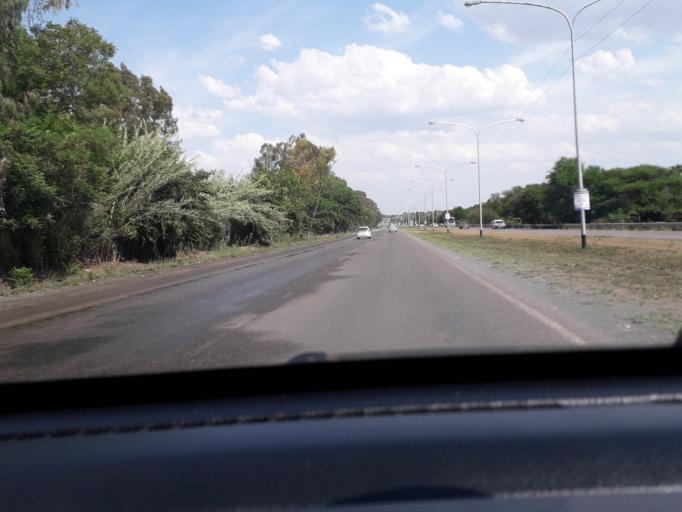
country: ZA
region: Gauteng
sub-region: City of Tshwane Metropolitan Municipality
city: Centurion
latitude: -25.8460
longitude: 28.2150
